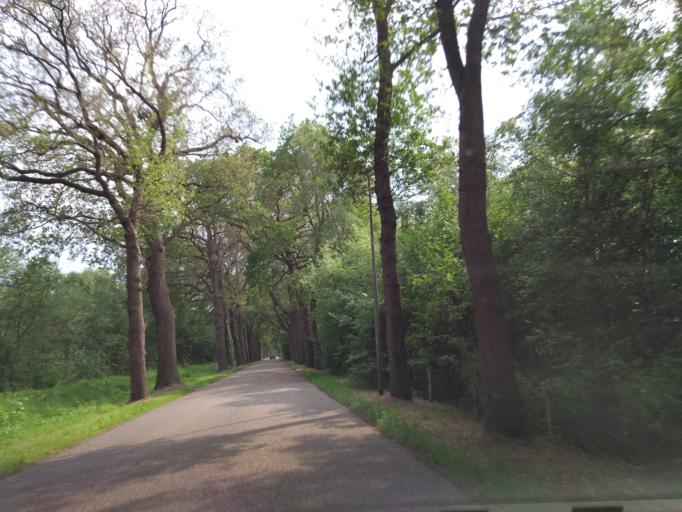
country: NL
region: Overijssel
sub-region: Gemeente Staphorst
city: Staphorst
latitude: 52.6476
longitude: 6.2890
